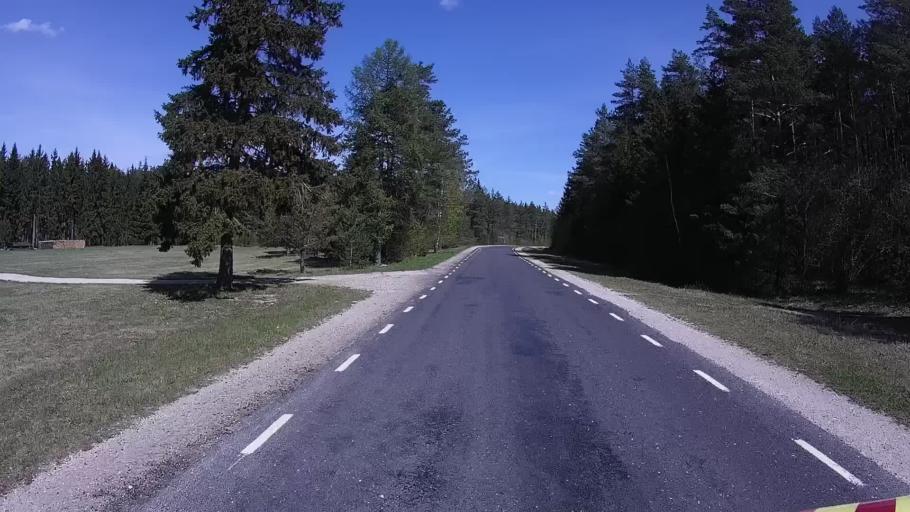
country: EE
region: Laeaene
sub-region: Ridala Parish
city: Uuemoisa
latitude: 59.0328
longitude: 23.8212
